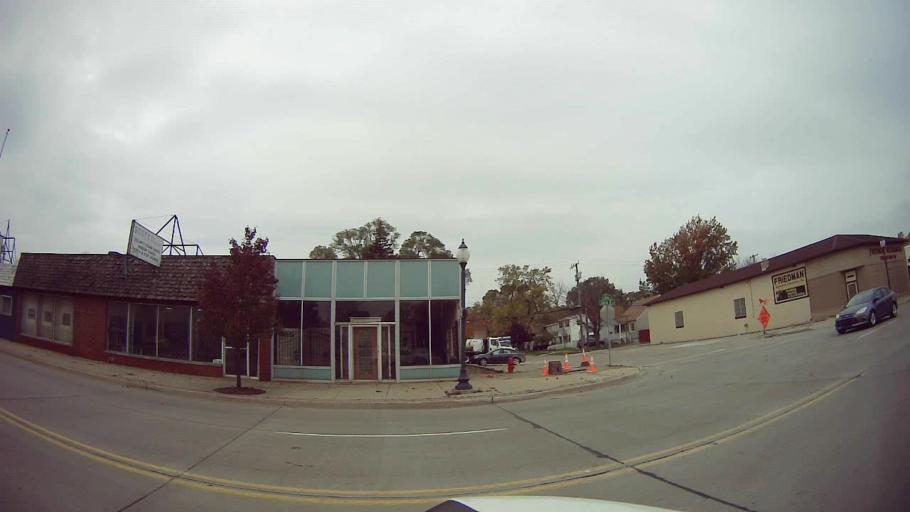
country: US
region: Michigan
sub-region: Oakland County
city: Hazel Park
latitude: 42.4731
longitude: -83.1044
